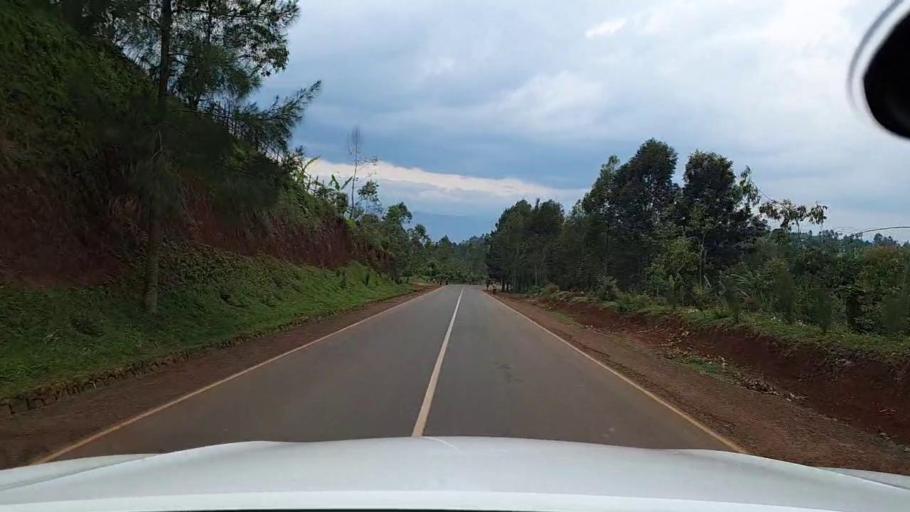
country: RW
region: Western Province
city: Cyangugu
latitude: -2.6450
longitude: 28.9550
